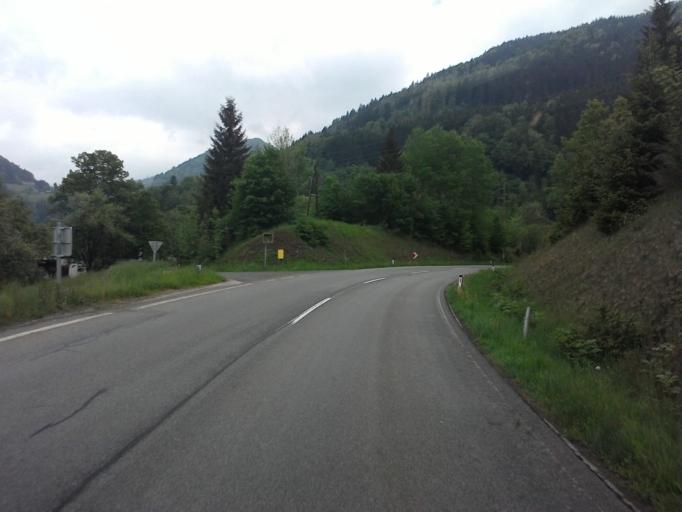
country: AT
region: Styria
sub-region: Politischer Bezirk Liezen
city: Altenmarkt bei Sankt Gallen
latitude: 47.7160
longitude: 14.6776
